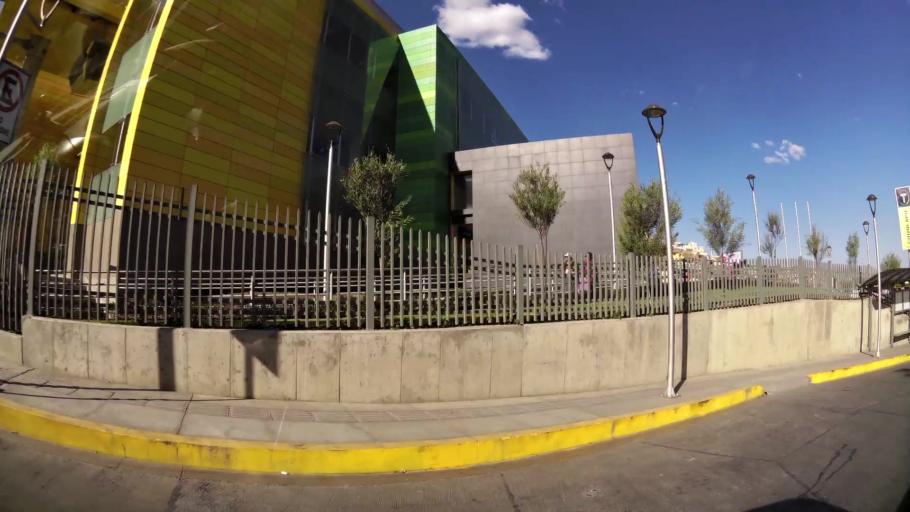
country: BO
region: La Paz
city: La Paz
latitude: -16.5192
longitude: -68.1164
